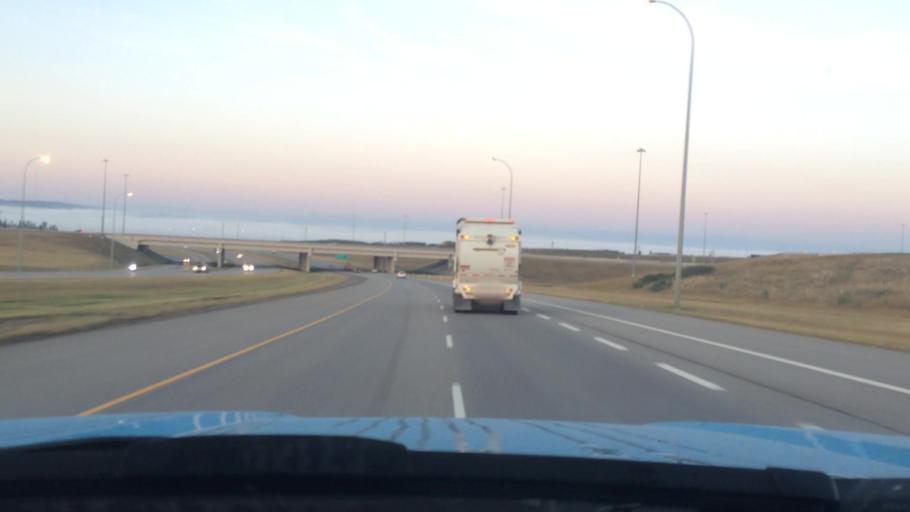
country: CA
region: Alberta
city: Calgary
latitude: 51.1345
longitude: -114.2242
